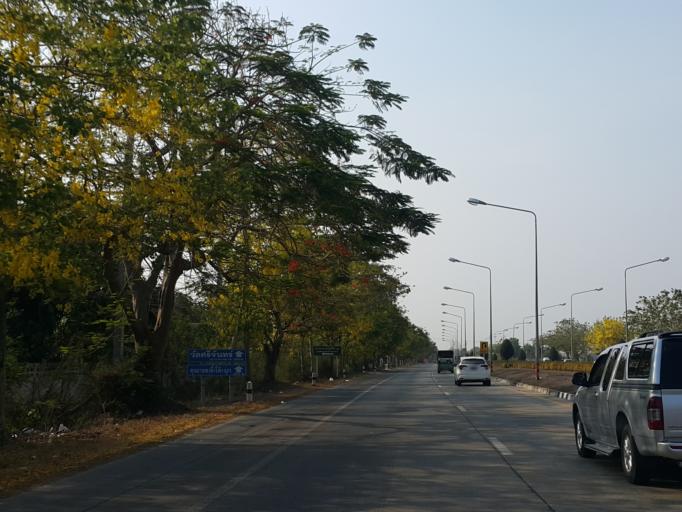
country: TH
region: Suphan Buri
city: Sam Chuk
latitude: 14.7662
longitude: 100.0929
